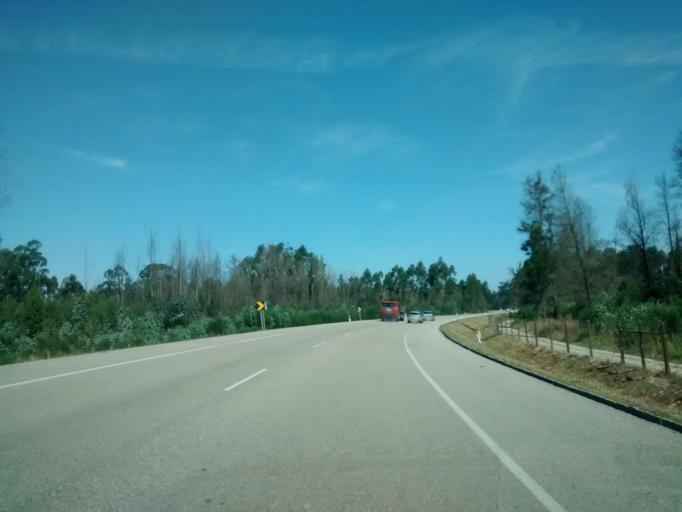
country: PT
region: Coimbra
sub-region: Mira
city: Mira
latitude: 40.4383
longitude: -8.7363
